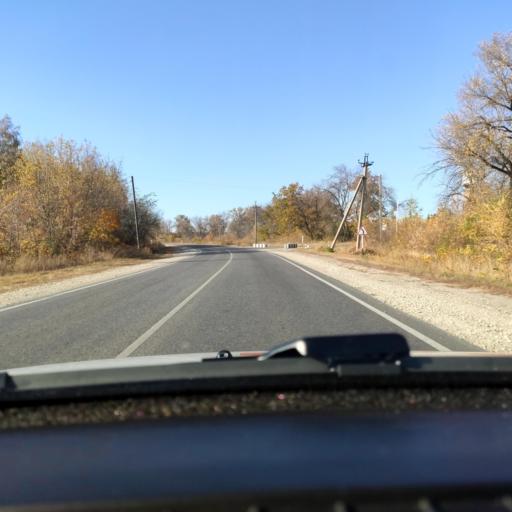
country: RU
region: Voronezj
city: Semiluki
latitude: 51.7274
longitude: 38.9872
